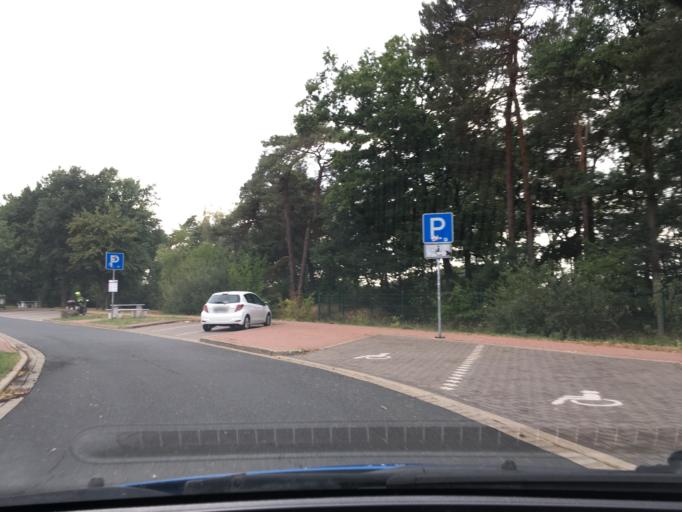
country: DE
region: Lower Saxony
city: Langenhagen
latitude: 52.5063
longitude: 9.7591
